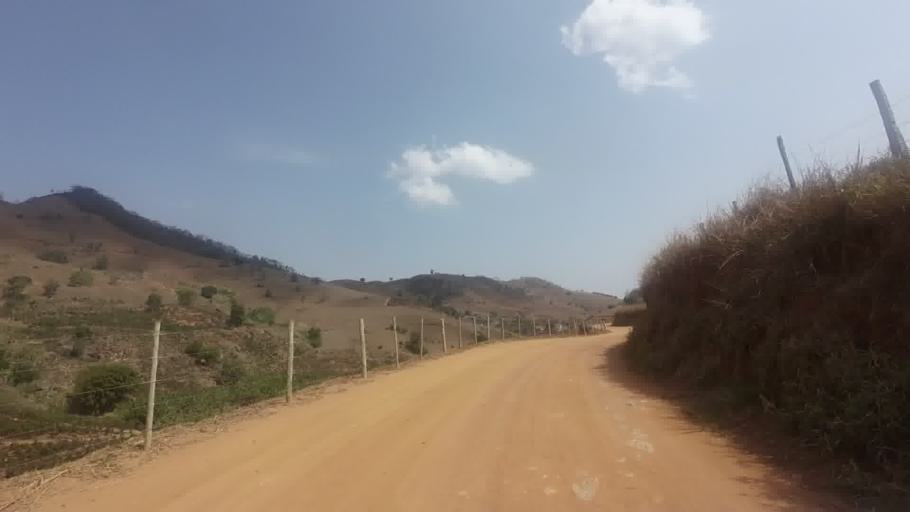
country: BR
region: Espirito Santo
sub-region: Sao Jose Do Calcado
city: Sao Jose do Calcado
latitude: -21.0480
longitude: -41.5232
